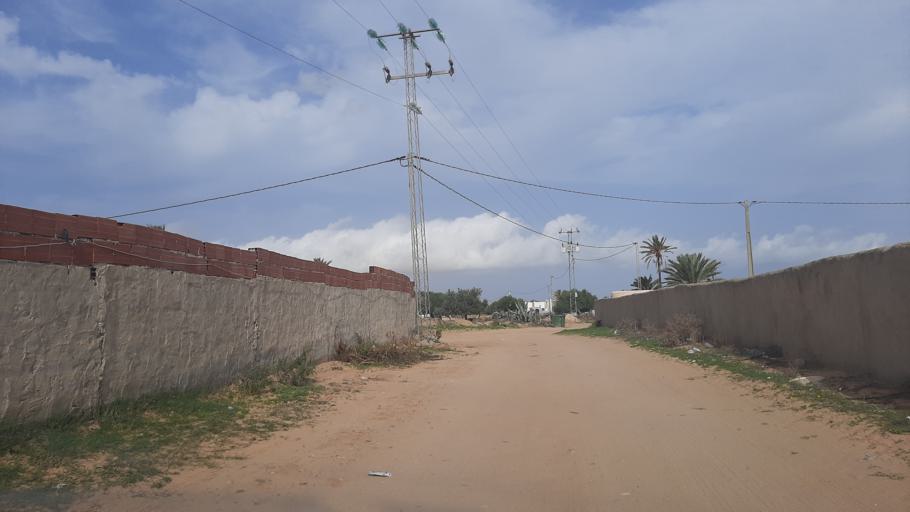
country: TN
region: Madanin
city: Midoun
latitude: 33.8035
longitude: 11.0259
